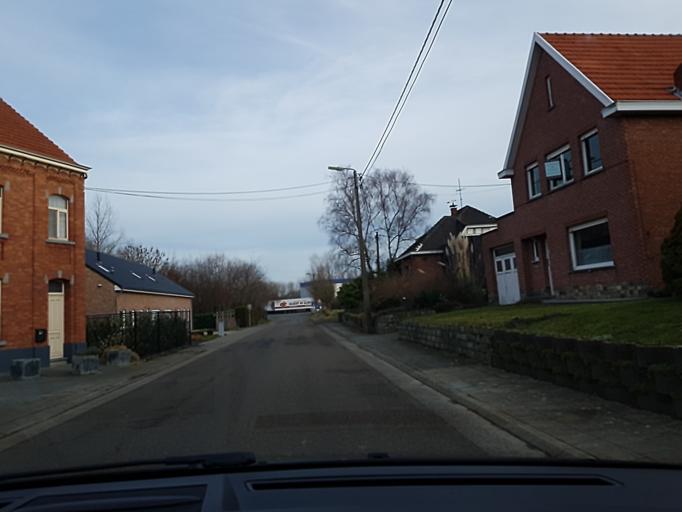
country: BE
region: Flanders
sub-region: Provincie Vlaams-Brabant
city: Rotselaar
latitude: 50.9422
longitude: 4.7245
